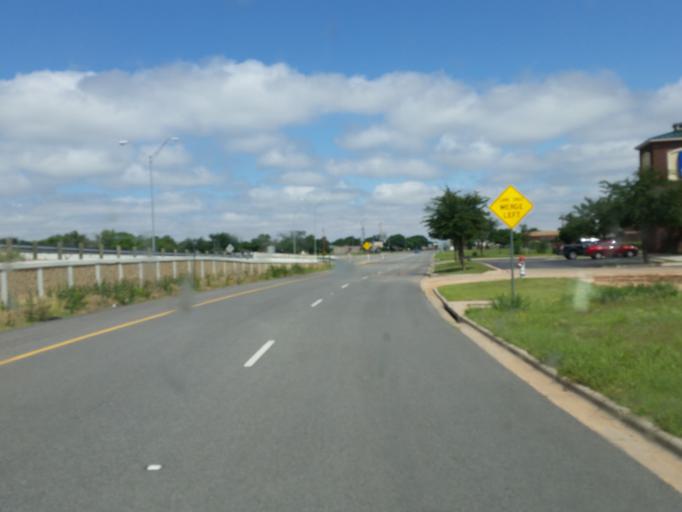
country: US
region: Texas
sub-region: Lubbock County
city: Lubbock
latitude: 33.5394
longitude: -101.8462
